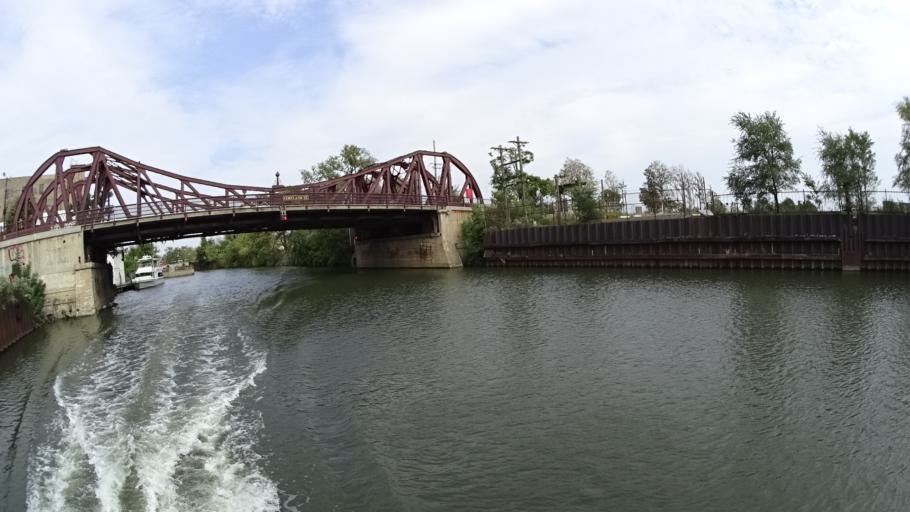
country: US
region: Illinois
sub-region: Cook County
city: Chicago
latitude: 41.9166
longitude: -87.6644
